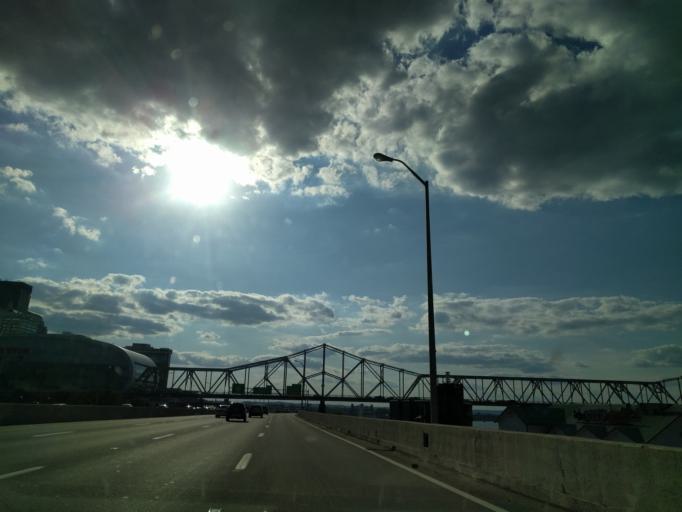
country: US
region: Kentucky
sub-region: Jefferson County
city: Louisville
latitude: 38.2591
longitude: -85.7484
